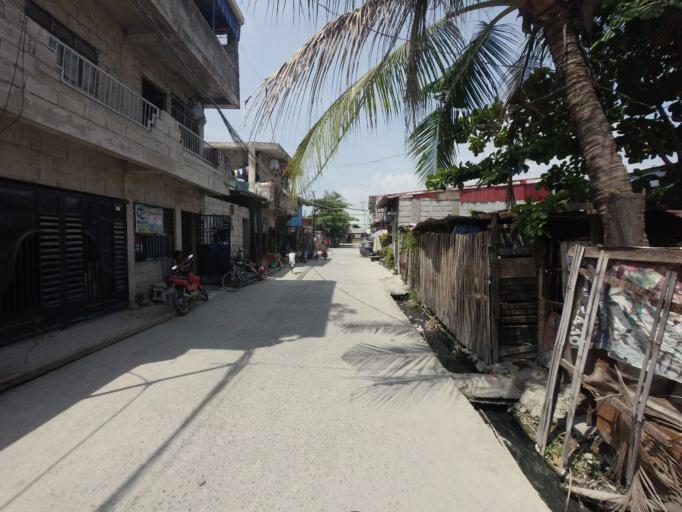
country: PH
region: Calabarzon
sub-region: Province of Rizal
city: Taytay
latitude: 14.5376
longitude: 121.1094
